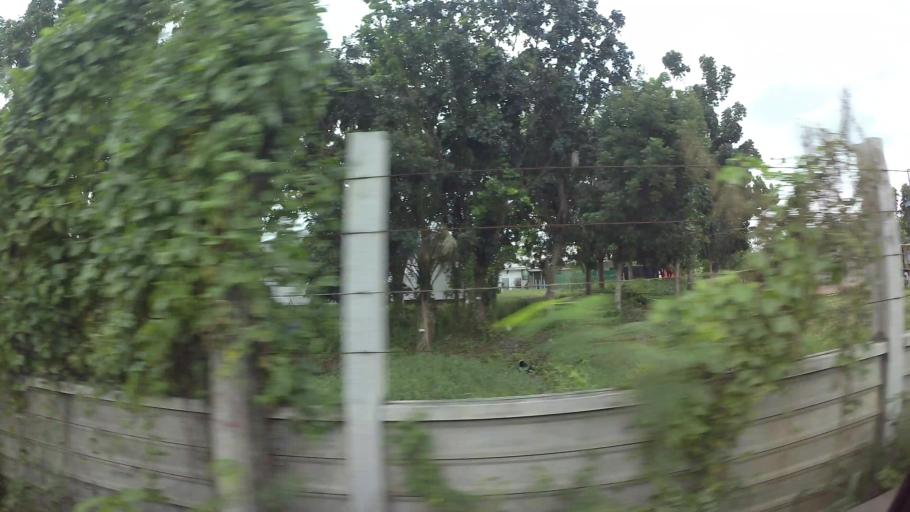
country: TH
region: Chon Buri
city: Si Racha
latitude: 13.1746
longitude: 100.9712
